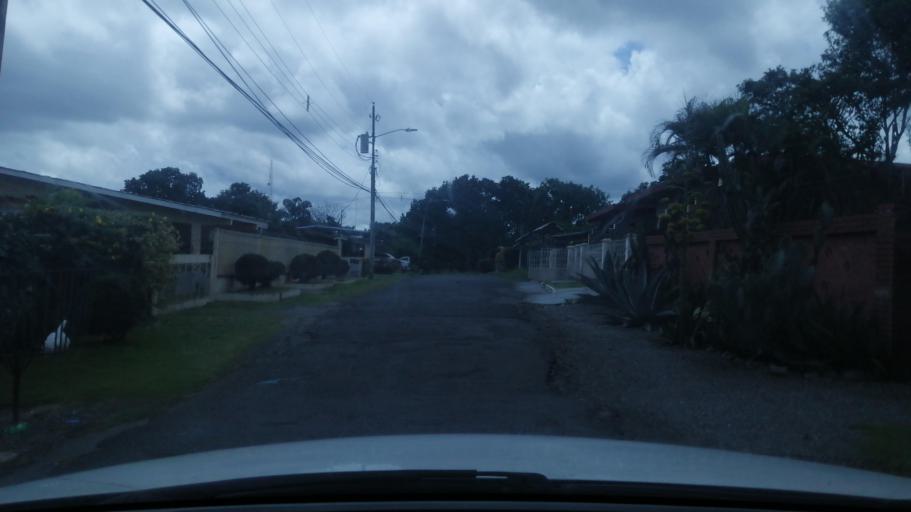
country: PA
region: Chiriqui
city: David
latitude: 8.4419
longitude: -82.4188
